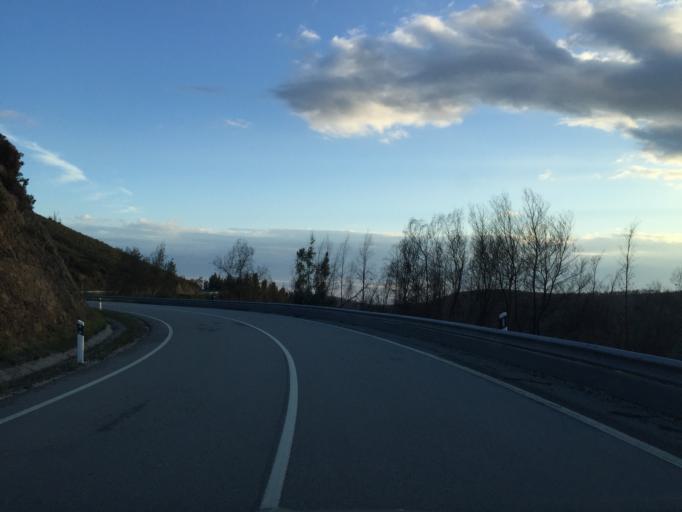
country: PT
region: Coimbra
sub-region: Pampilhosa da Serra
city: Pampilhosa da Serra
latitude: 40.0933
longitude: -7.9894
